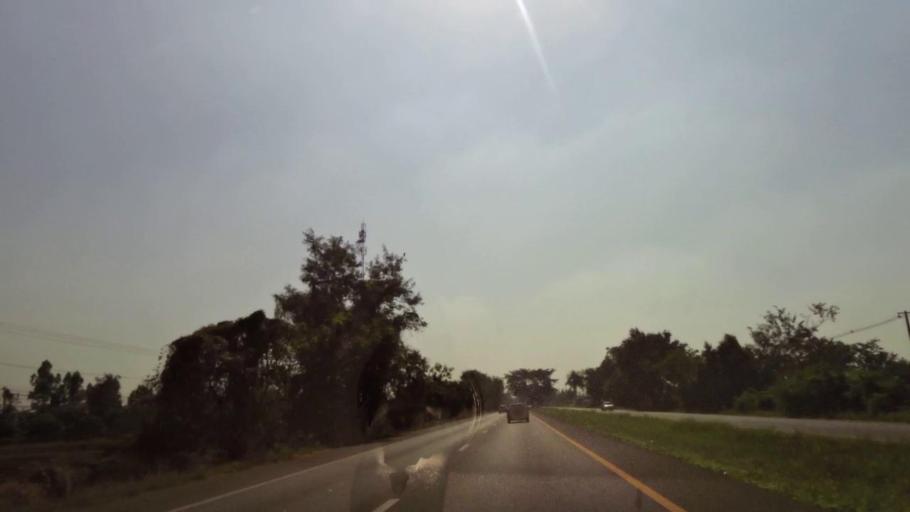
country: TH
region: Phichit
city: Bueng Na Rang
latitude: 16.0407
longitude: 100.1180
